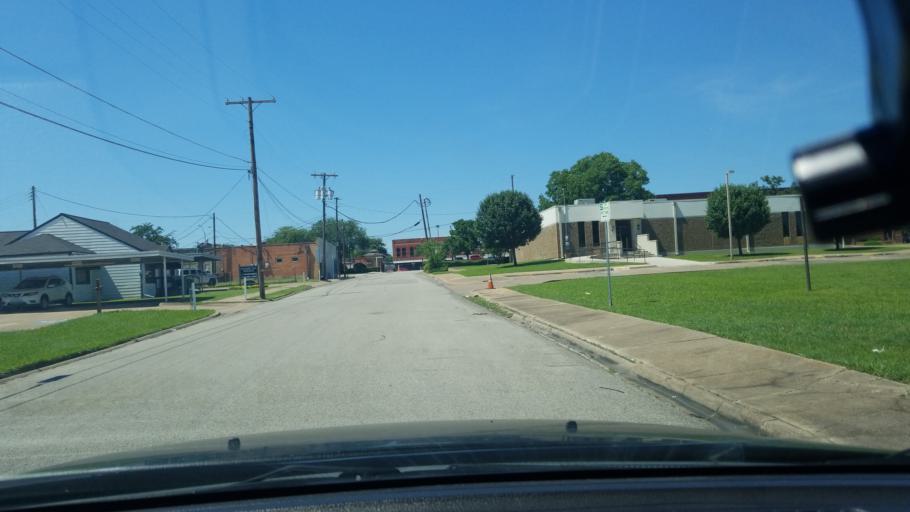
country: US
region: Texas
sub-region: Dallas County
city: Mesquite
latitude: 32.7654
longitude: -96.6006
